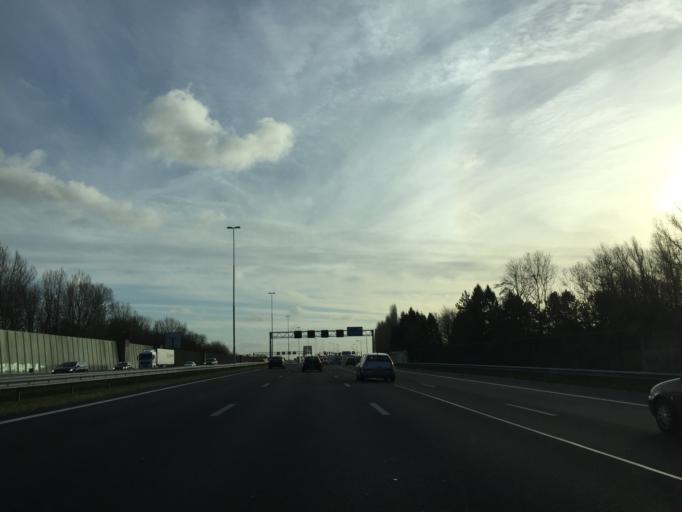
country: NL
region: Utrecht
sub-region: Gemeente Nieuwegein
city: Nieuwegein
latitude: 52.0091
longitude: 5.0721
